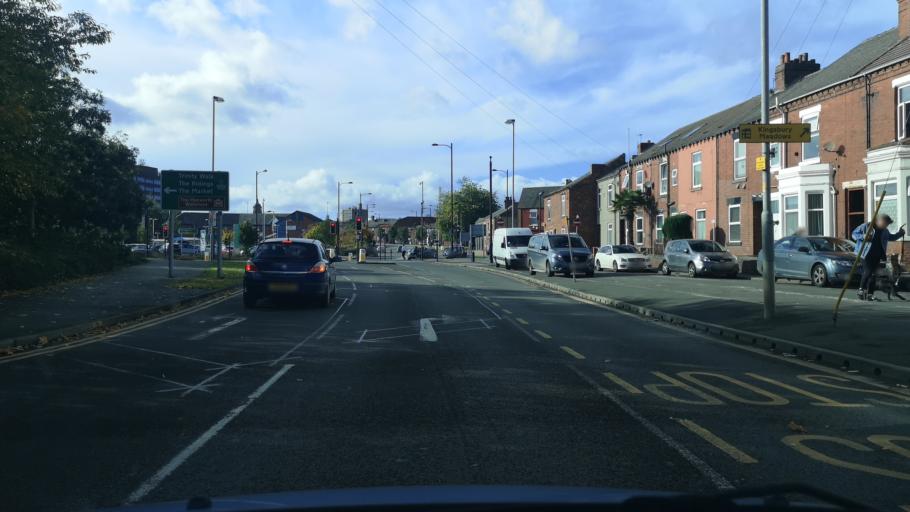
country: GB
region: England
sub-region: City and Borough of Wakefield
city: Wakefield
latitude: 53.6868
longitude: -1.4917
